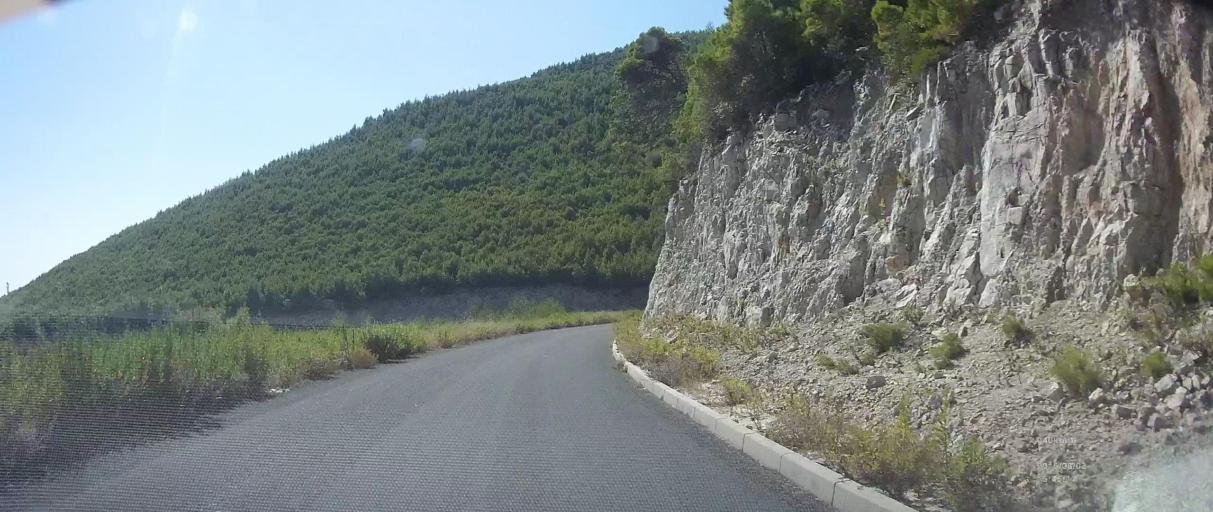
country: HR
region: Dubrovacko-Neretvanska
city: Blato
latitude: 42.7378
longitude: 17.5198
